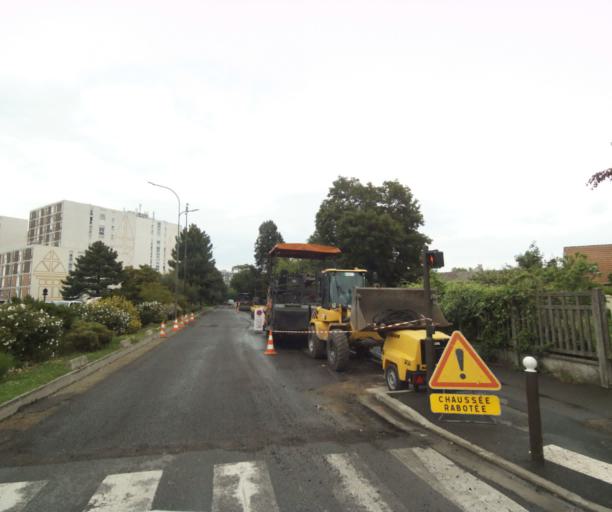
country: FR
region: Ile-de-France
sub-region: Departement du Val-d'Oise
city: Argenteuil
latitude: 48.9433
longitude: 2.2303
